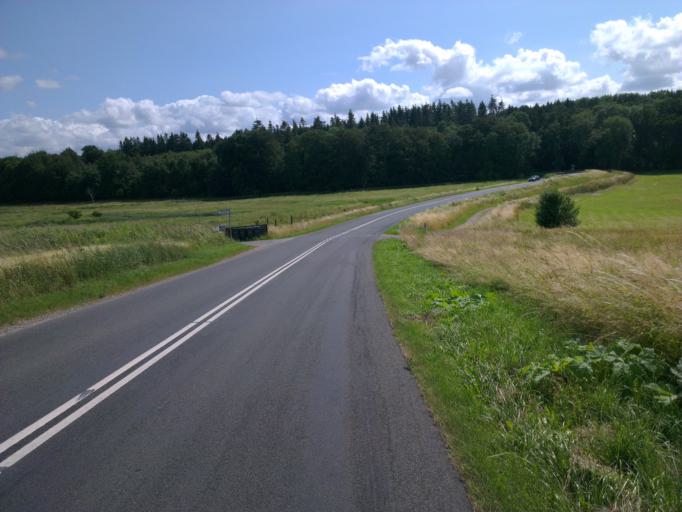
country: DK
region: Zealand
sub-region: Lejre Kommune
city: Ejby
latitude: 55.7385
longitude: 11.8824
